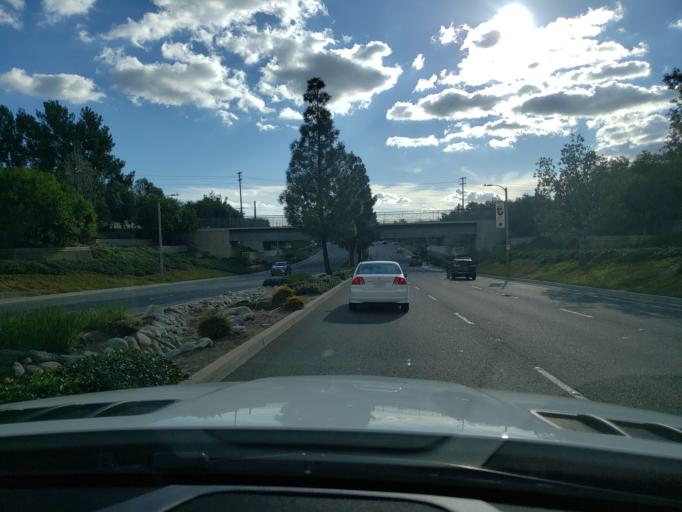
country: US
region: California
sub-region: San Bernardino County
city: Rancho Cucamonga
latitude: 34.0930
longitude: -117.5569
